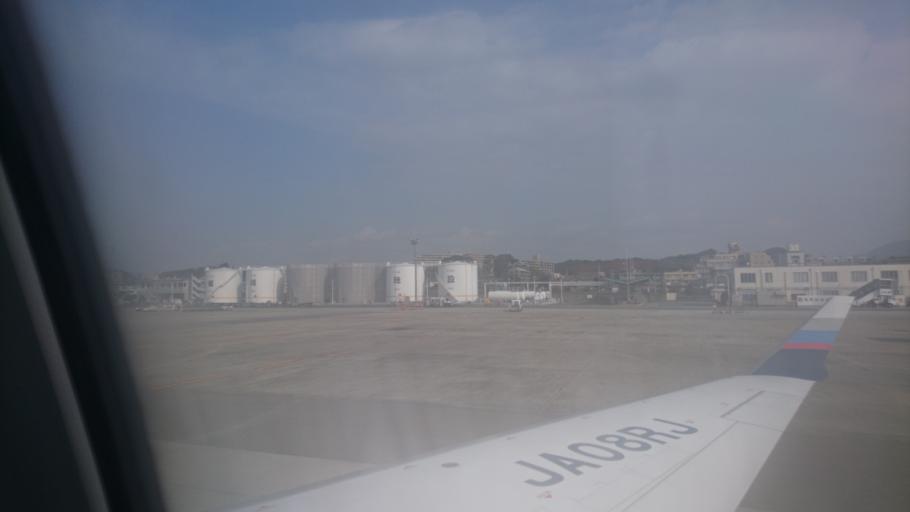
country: JP
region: Fukuoka
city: Fukuoka-shi
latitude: 33.5890
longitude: 130.4509
